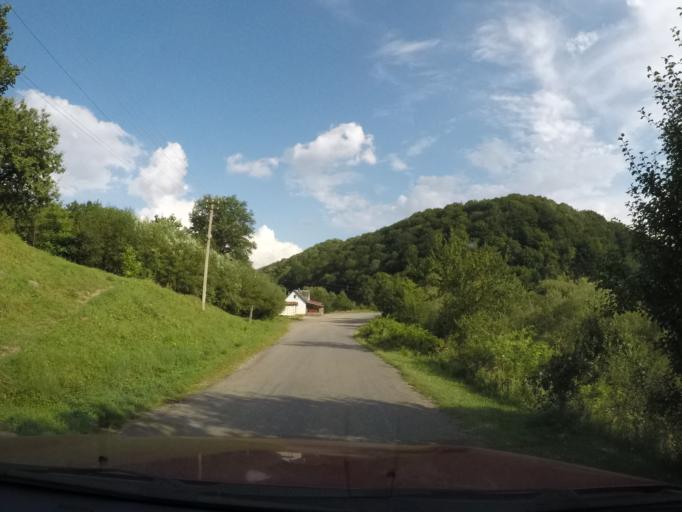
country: UA
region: Zakarpattia
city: Velykyi Bereznyi
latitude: 49.0044
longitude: 22.6391
